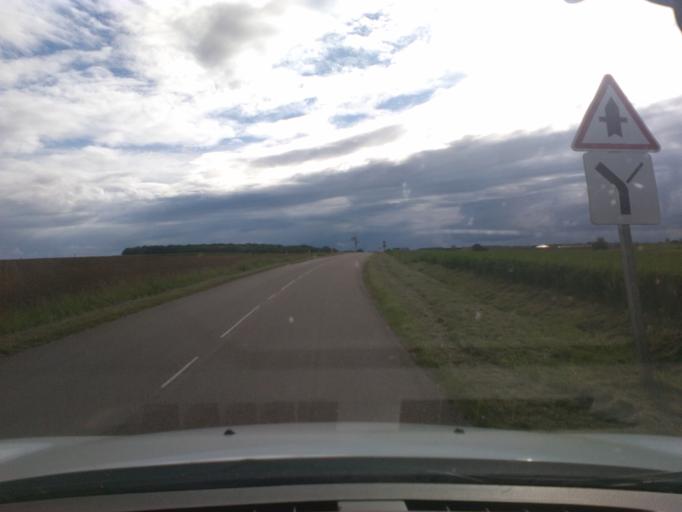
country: FR
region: Lorraine
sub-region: Departement des Vosges
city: Mirecourt
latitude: 48.3292
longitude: 6.0446
